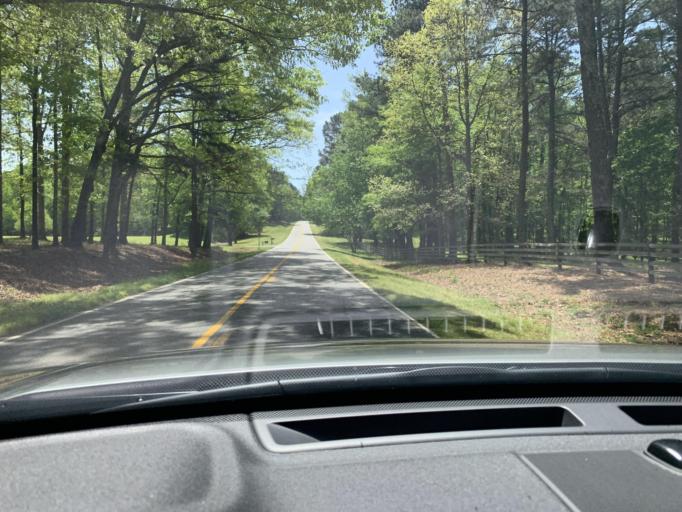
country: US
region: Georgia
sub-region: Oconee County
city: Bogart
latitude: 33.8827
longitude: -83.5563
